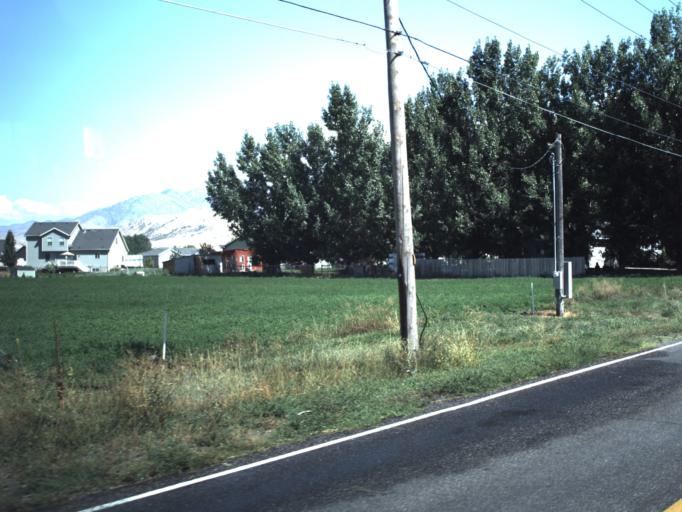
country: US
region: Utah
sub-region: Cache County
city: Smithfield
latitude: 41.8386
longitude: -111.8524
